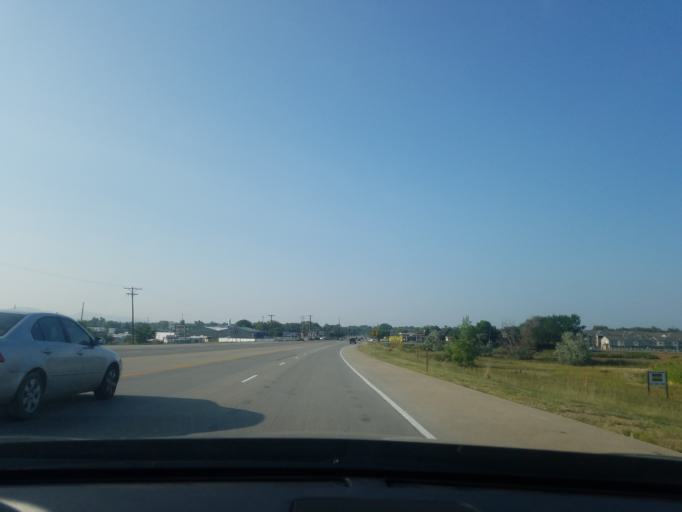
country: US
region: Colorado
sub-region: Larimer County
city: Loveland
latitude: 40.3755
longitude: -105.0730
